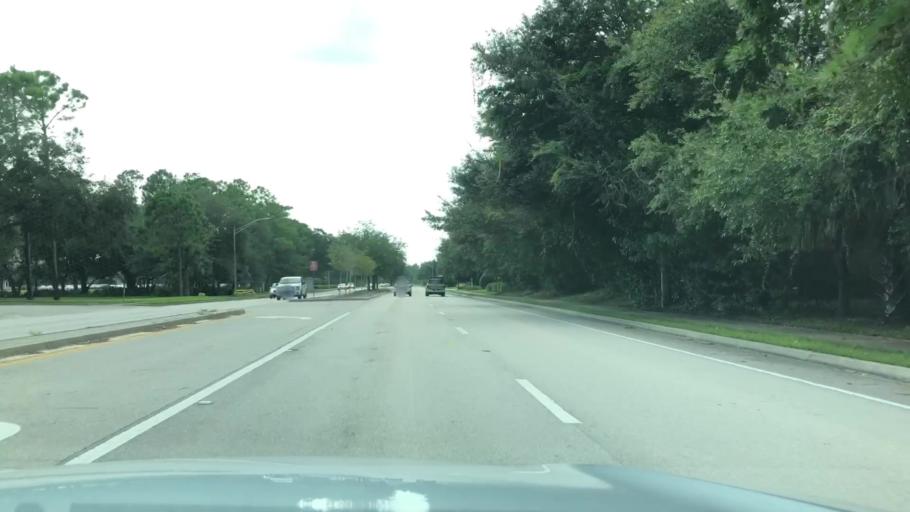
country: US
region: Florida
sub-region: Duval County
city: Jacksonville Beach
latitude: 30.2660
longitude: -81.4394
